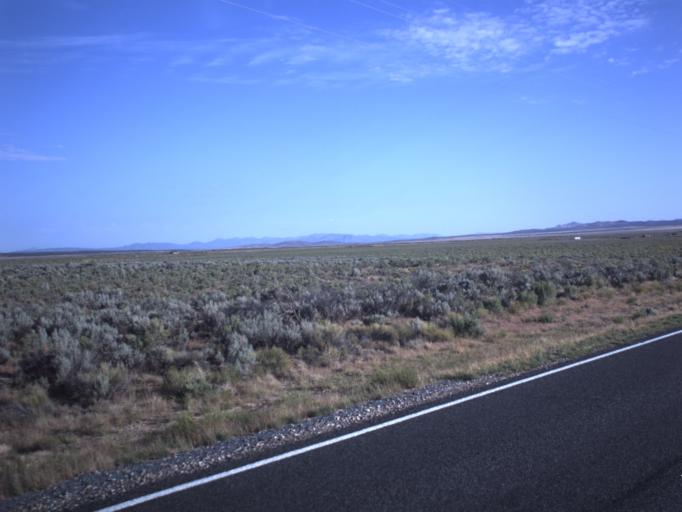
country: US
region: Utah
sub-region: Iron County
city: Enoch
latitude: 37.8245
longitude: -113.0504
